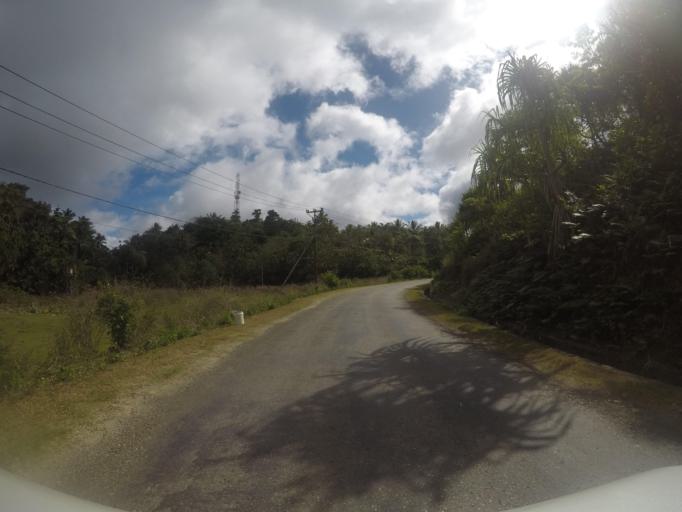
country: TL
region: Lautem
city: Lospalos
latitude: -8.5431
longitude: 126.9466
